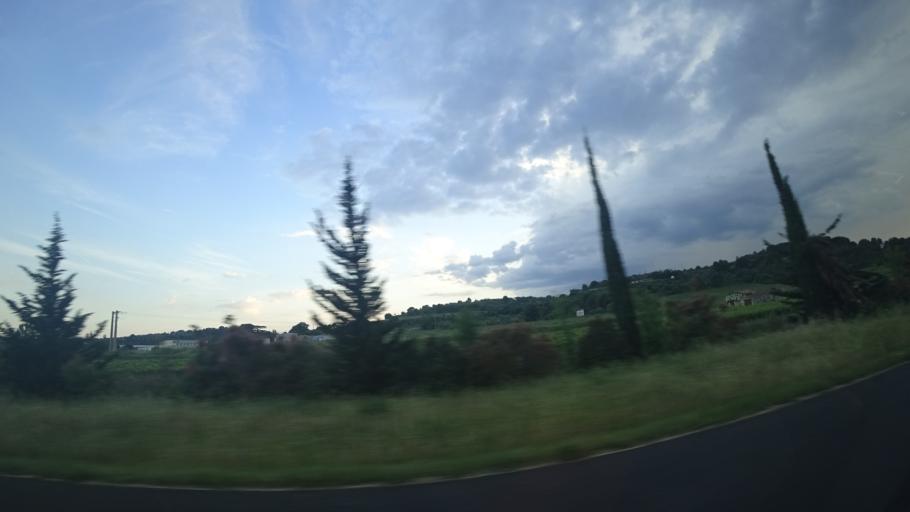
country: FR
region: Languedoc-Roussillon
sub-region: Departement de l'Herault
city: Nebian
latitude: 43.6239
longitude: 3.4528
